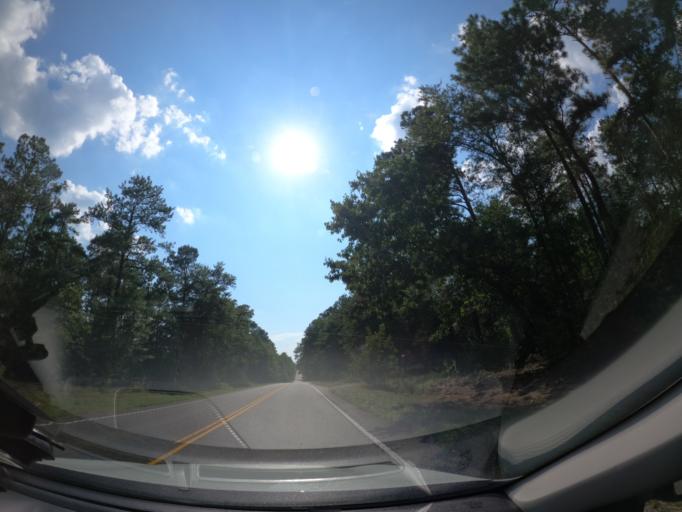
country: US
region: South Carolina
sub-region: Aiken County
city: New Ellenton
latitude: 33.3895
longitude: -81.5762
